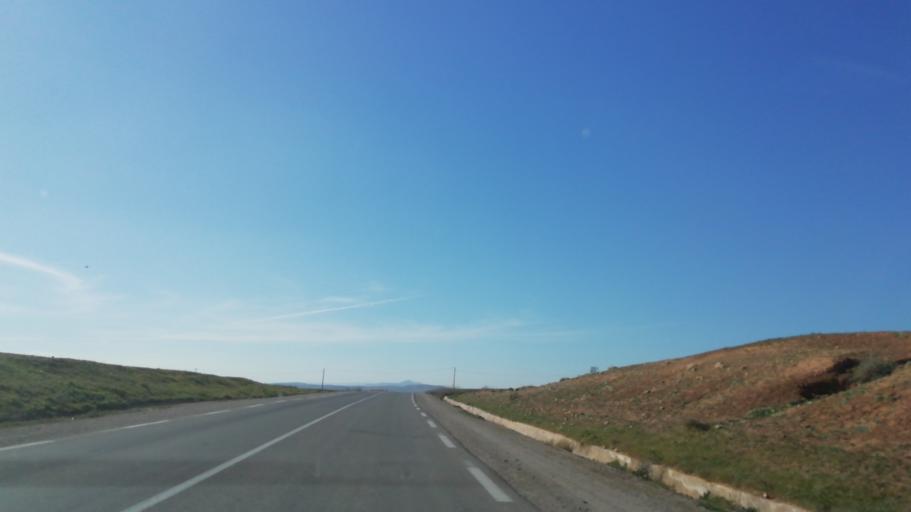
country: DZ
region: Mascara
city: Oued el Abtal
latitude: 35.4542
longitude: 0.7701
